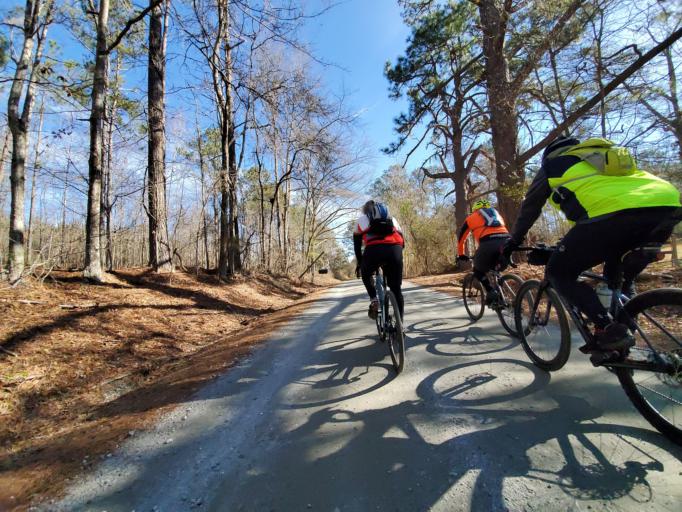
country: US
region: Georgia
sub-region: Fulton County
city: Chattahoochee Hills
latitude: 33.5745
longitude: -84.7790
